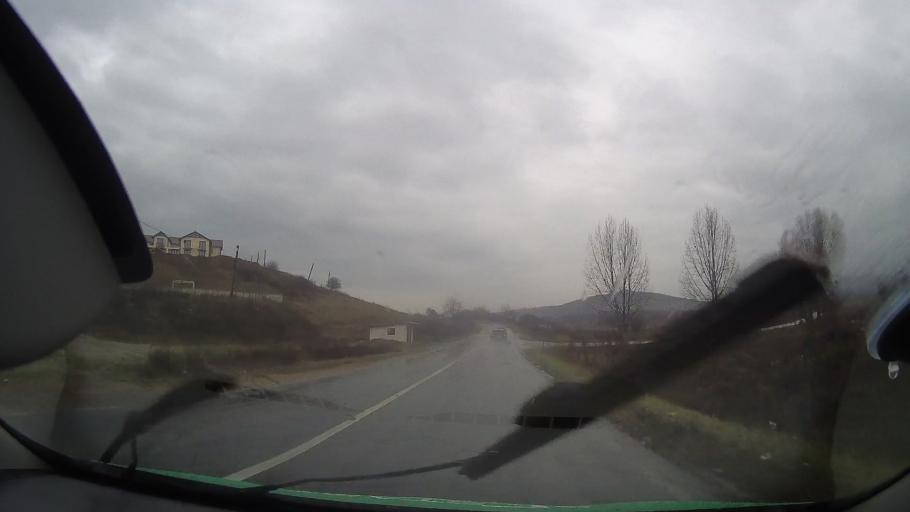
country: RO
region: Bihor
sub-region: Comuna Rabagani
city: Rabagani
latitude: 46.7544
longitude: 22.2066
